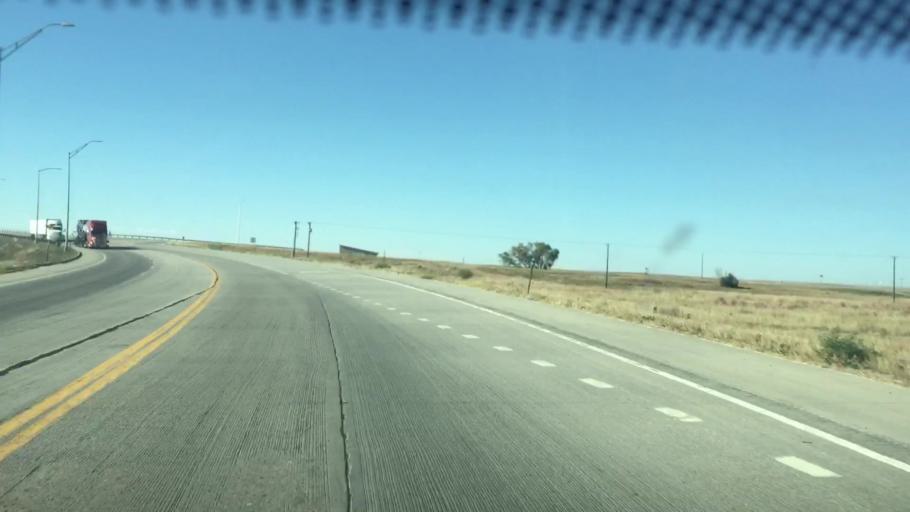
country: US
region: Colorado
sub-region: Kiowa County
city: Eads
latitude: 38.7609
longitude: -102.7775
